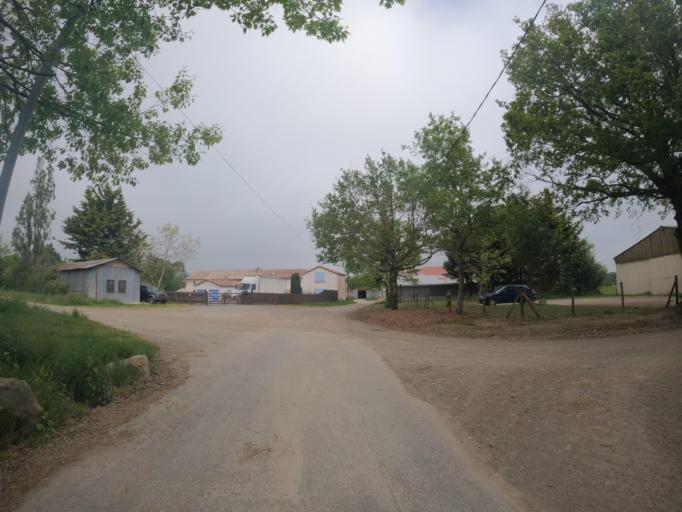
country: FR
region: Poitou-Charentes
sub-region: Departement des Deux-Sevres
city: Chiche
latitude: 46.8427
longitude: -0.3833
